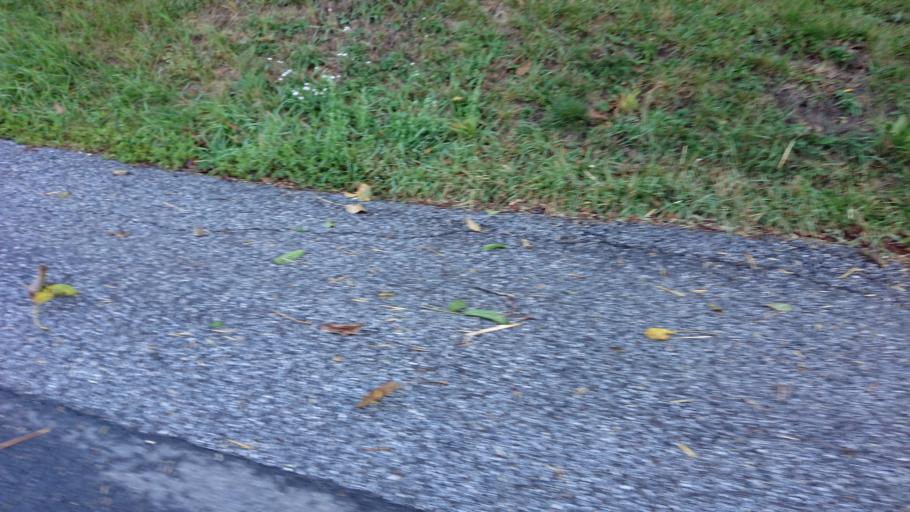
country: IT
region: Trentino-Alto Adige
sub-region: Bolzano
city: Campo di Trens
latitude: 46.8753
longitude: 11.4872
